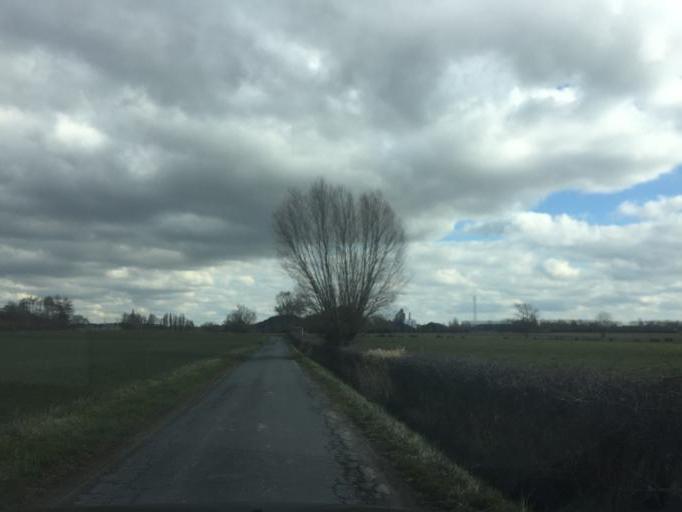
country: BE
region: Flanders
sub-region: Provincie West-Vlaanderen
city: Lichtervelde
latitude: 50.9931
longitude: 3.1568
